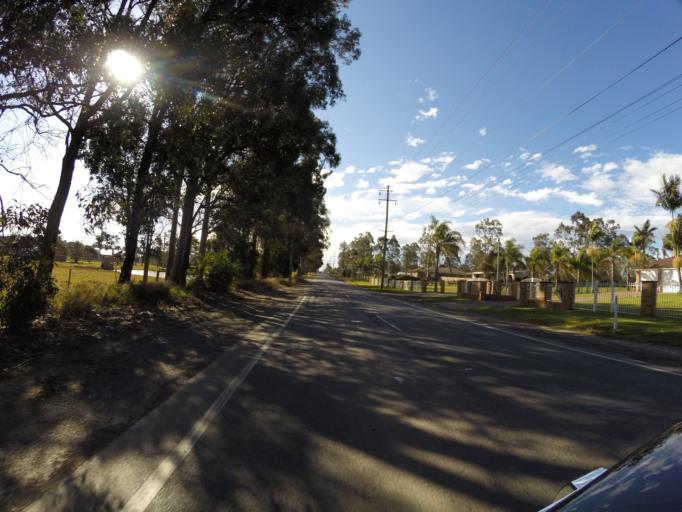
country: AU
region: New South Wales
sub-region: Fairfield
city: Cecil Park
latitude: -33.8982
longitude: 150.7894
